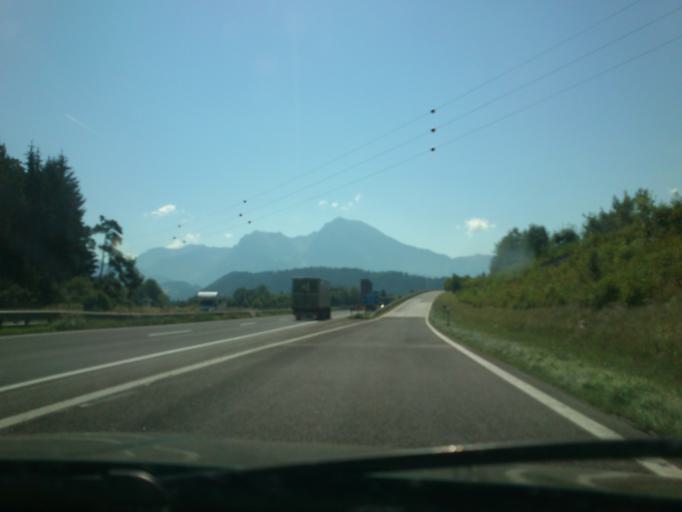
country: AT
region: Upper Austria
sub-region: Politischer Bezirk Kirchdorf an der Krems
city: Rossleithen
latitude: 47.7300
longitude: 14.2973
